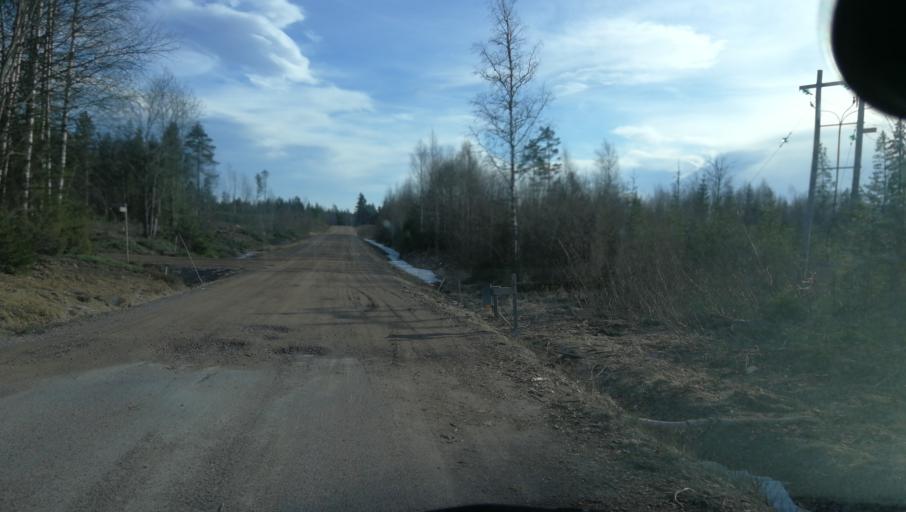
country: SE
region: Dalarna
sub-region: Vansbro Kommun
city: Vansbro
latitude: 60.8272
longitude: 14.1942
